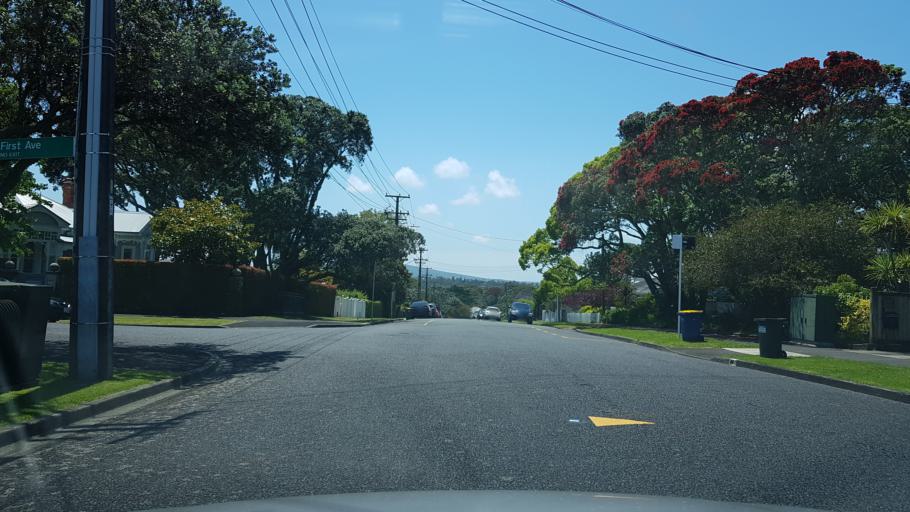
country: NZ
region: Auckland
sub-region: Auckland
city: North Shore
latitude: -36.8263
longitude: 174.7770
